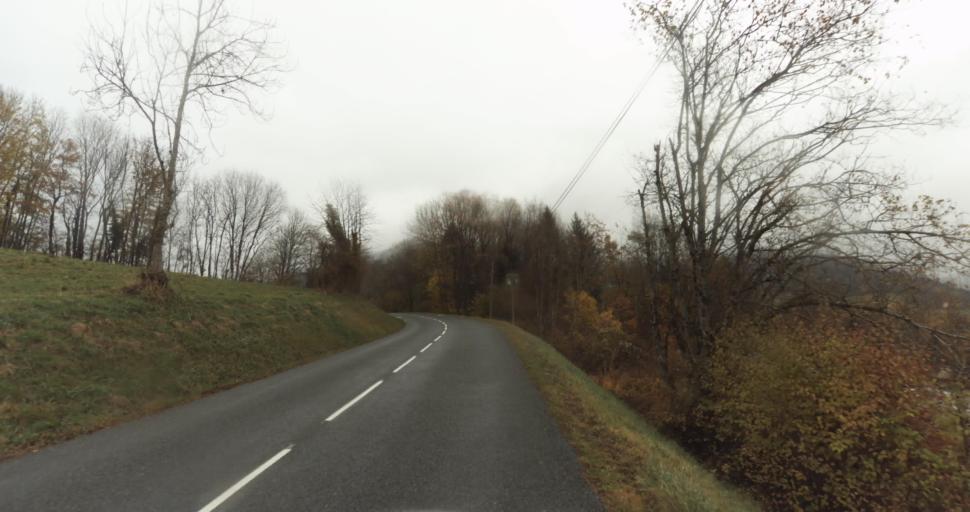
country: FR
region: Rhone-Alpes
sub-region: Departement de la Haute-Savoie
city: Thorens-Glieres
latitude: 46.0009
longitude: 6.2539
